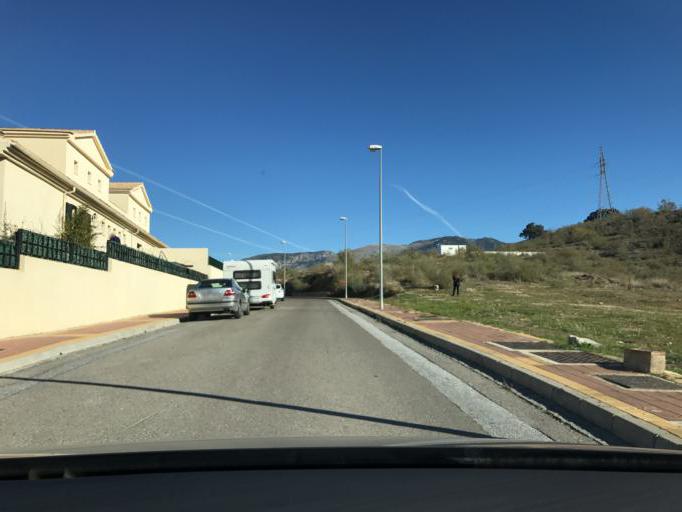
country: ES
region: Andalusia
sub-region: Provincia de Granada
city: Jun
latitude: 37.2102
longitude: -3.5890
